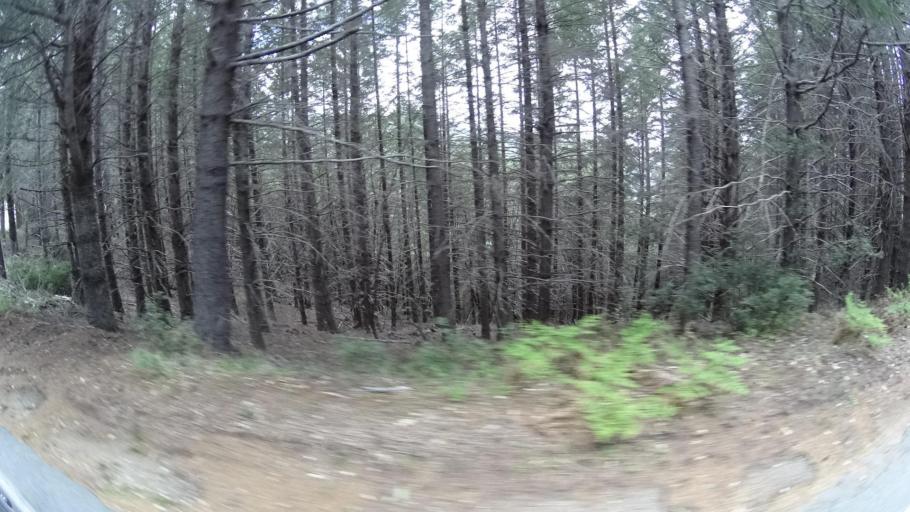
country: US
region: California
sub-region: Humboldt County
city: Redway
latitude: 40.0497
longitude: -124.0092
